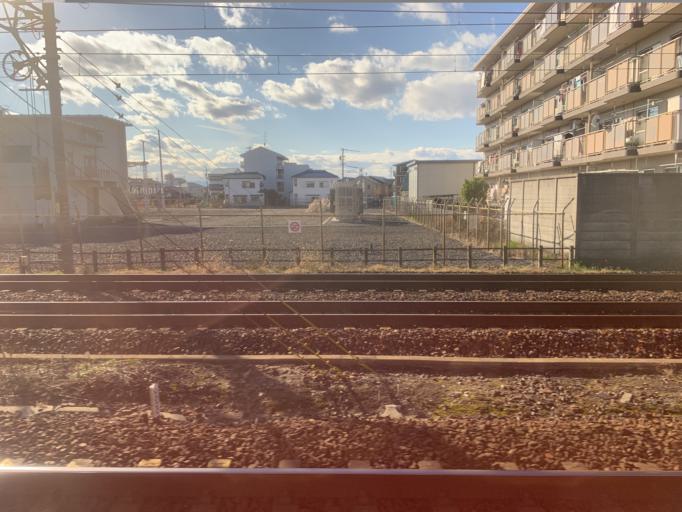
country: JP
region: Aichi
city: Ichinomiya
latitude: 35.3137
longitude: 136.7916
